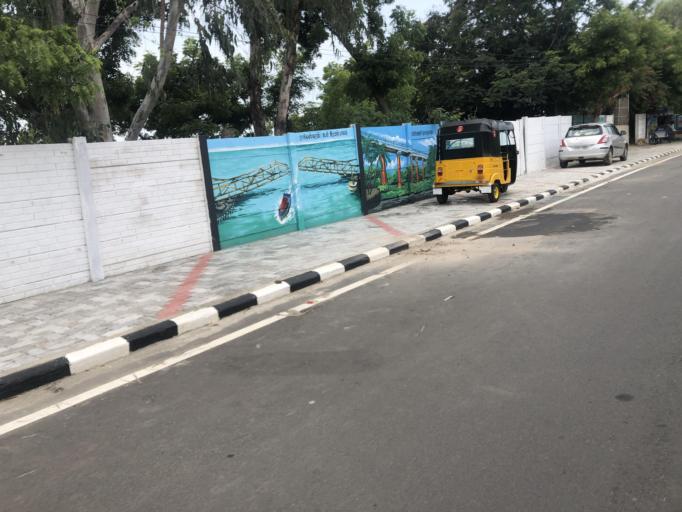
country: IN
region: Tamil Nadu
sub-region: Kancheepuram
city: Mamallapuram
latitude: 12.6122
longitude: 80.1907
